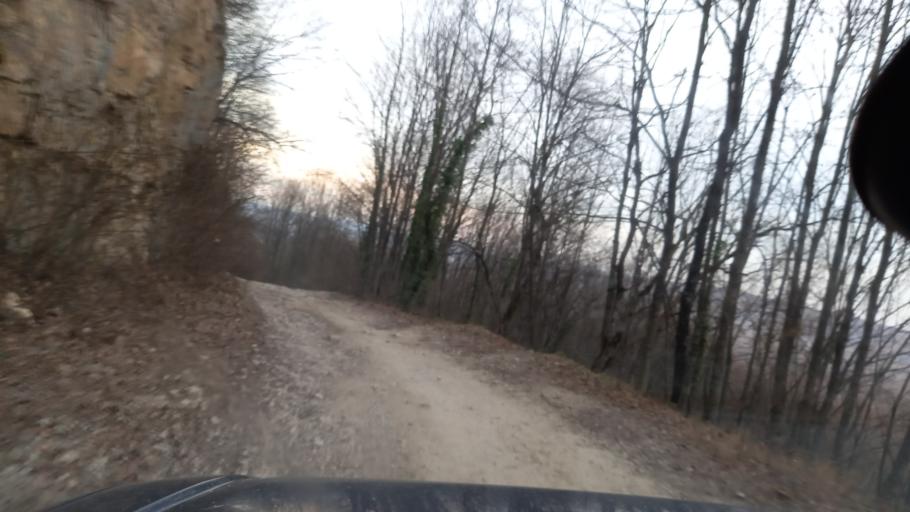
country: RU
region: Krasnodarskiy
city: Neftegorsk
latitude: 44.2203
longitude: 39.8978
